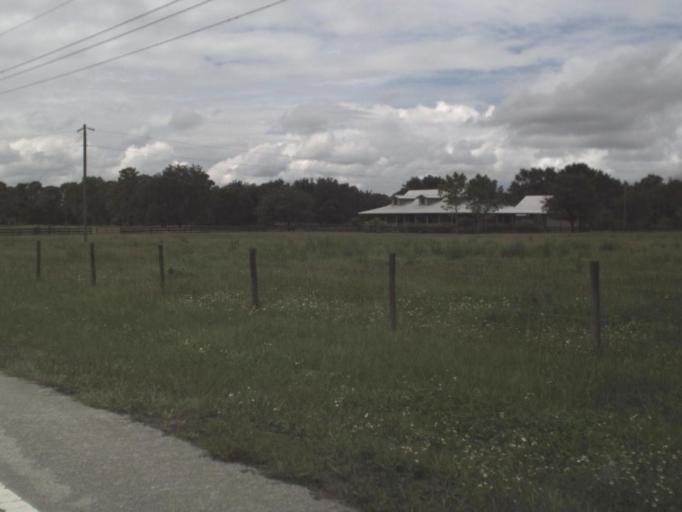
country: US
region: Florida
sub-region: Hardee County
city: Bowling Green
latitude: 27.5948
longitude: -81.8796
